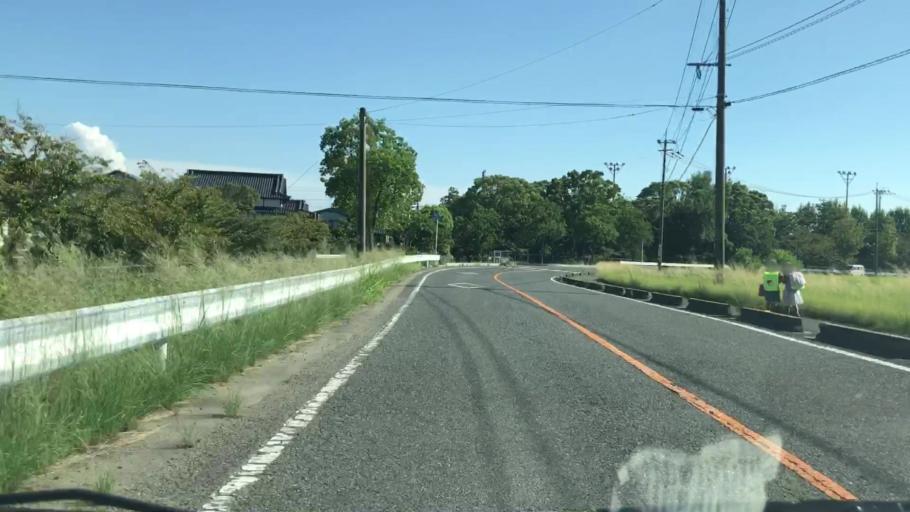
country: JP
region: Saga Prefecture
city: Okawa
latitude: 33.2285
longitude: 130.3558
